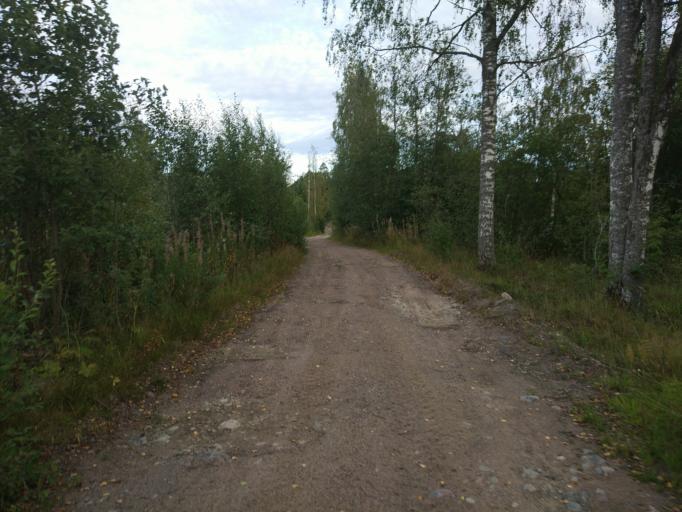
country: RU
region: Leningrad
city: Kuznechnoye
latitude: 61.1173
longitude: 29.6015
